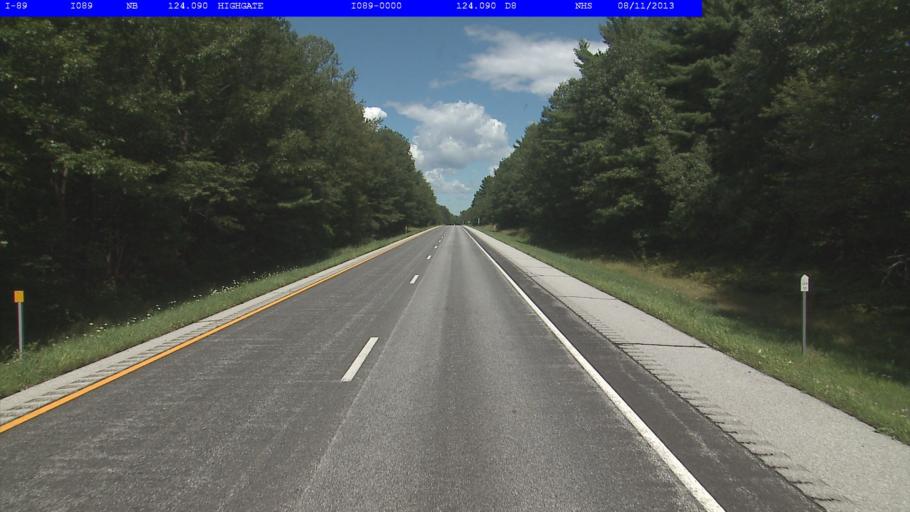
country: US
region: Vermont
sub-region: Franklin County
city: Swanton
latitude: 44.9323
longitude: -73.1118
